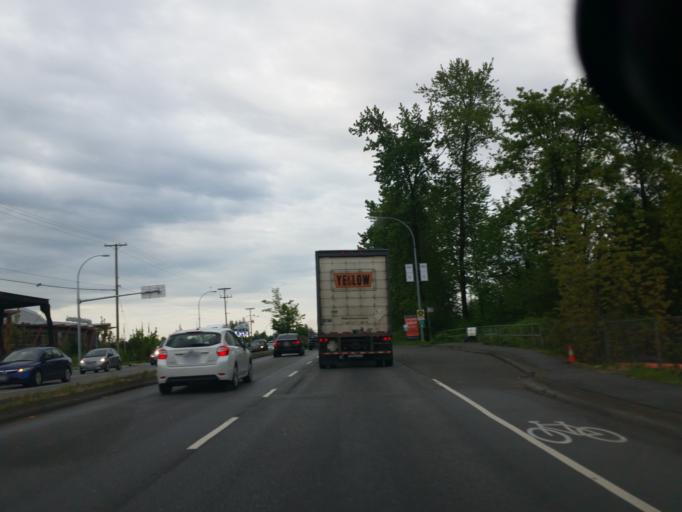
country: CA
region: British Columbia
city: Walnut Grove
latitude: 49.1480
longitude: -122.6684
